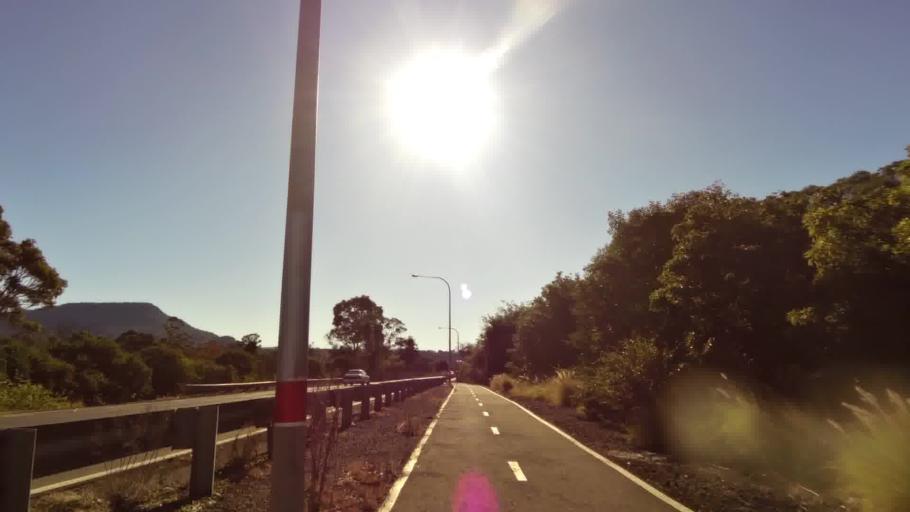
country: AU
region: New South Wales
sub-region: Wollongong
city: Koonawarra
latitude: -34.4815
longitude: 150.8037
